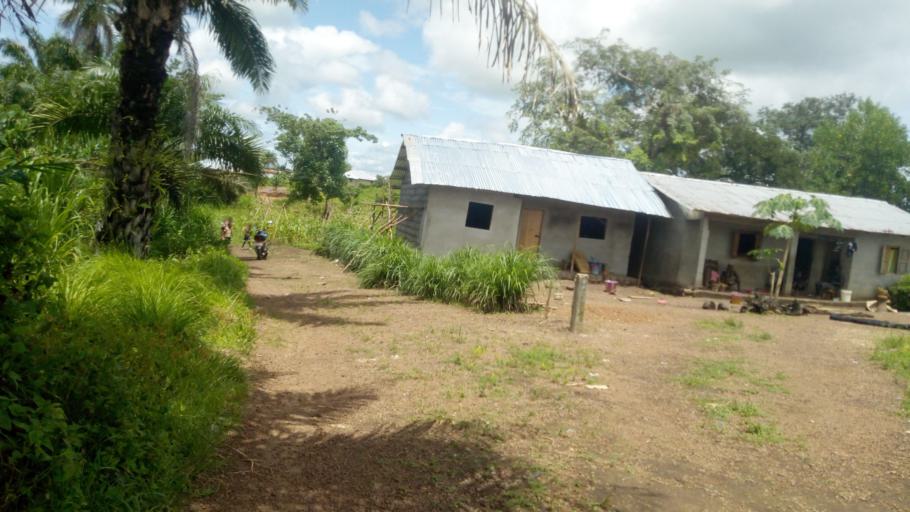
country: SL
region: Northern Province
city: Magburaka
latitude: 8.7135
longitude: -11.9531
